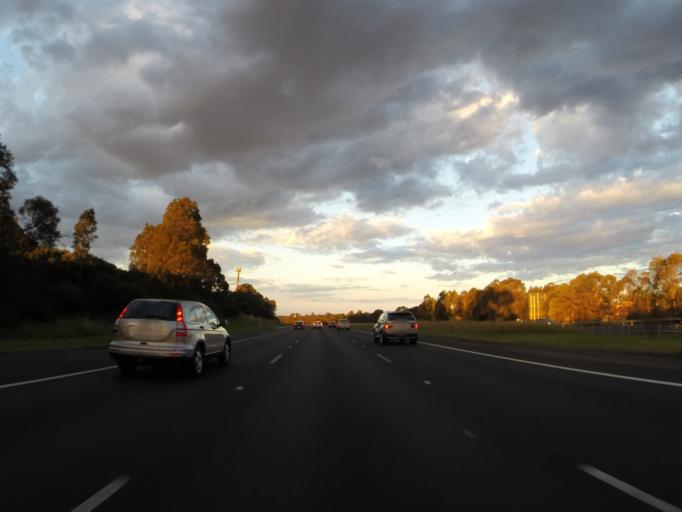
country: AU
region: New South Wales
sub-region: Campbelltown Municipality
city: Campbelltown
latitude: -34.0526
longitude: 150.8092
